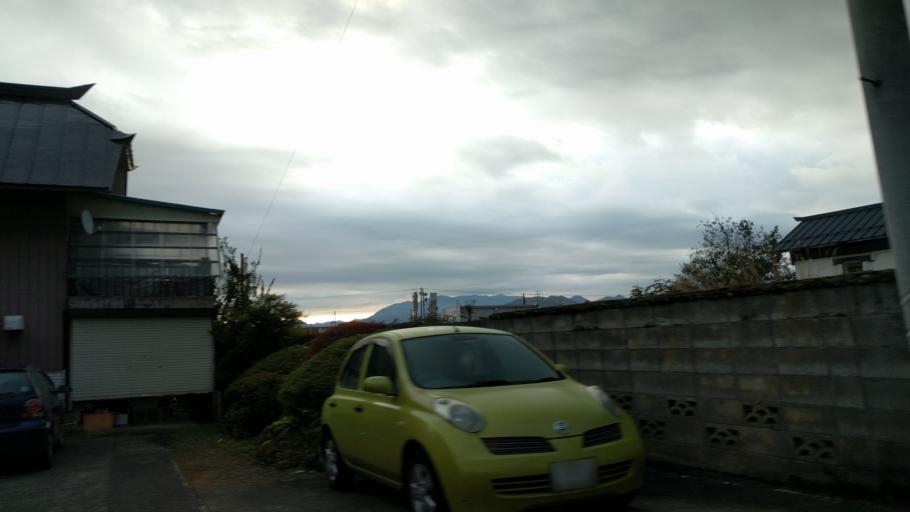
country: JP
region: Fukushima
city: Kitakata
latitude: 37.4507
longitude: 139.8335
